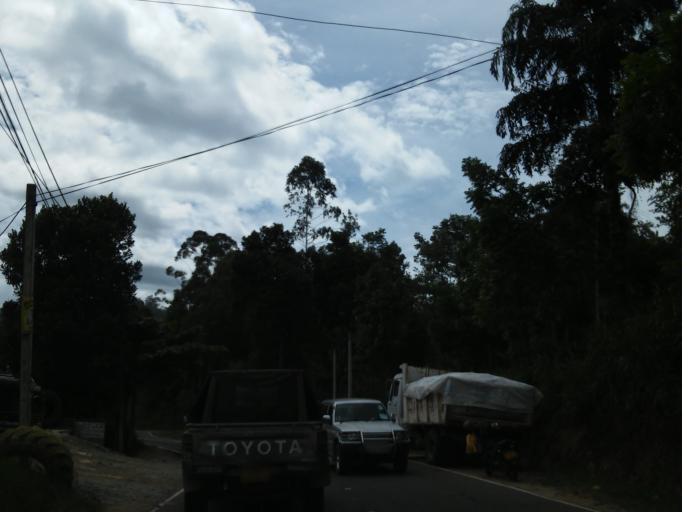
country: LK
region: Uva
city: Haputale
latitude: 6.8685
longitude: 80.9481
